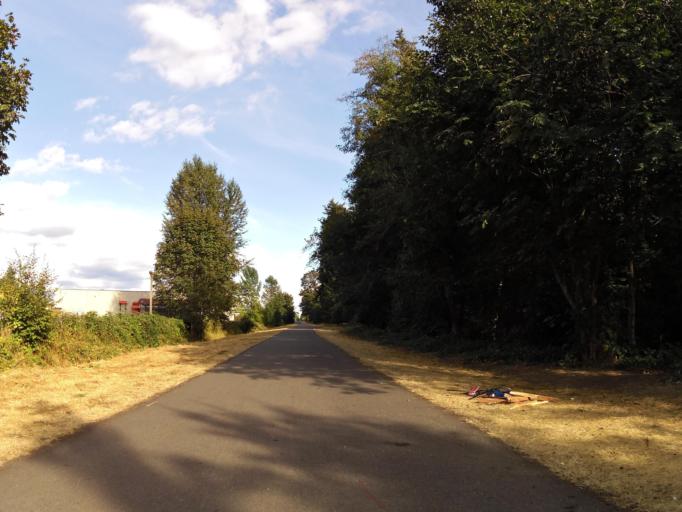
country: US
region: Washington
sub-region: Thurston County
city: Lacey
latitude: 47.0395
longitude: -122.8429
